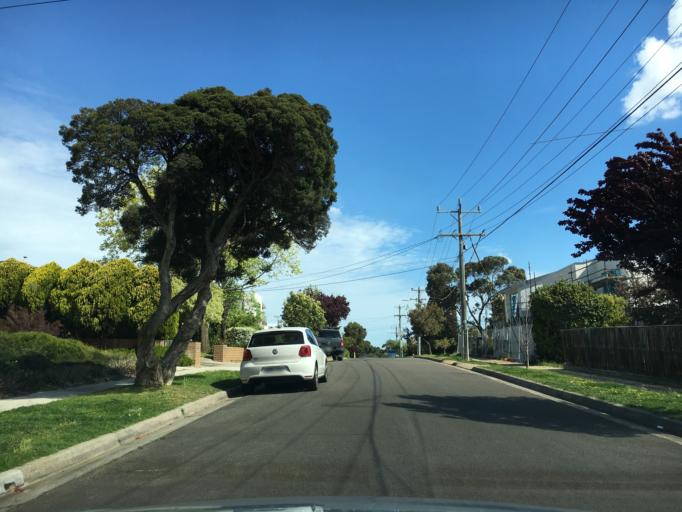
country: AU
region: Victoria
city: Clayton
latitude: -37.8960
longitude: 145.1184
